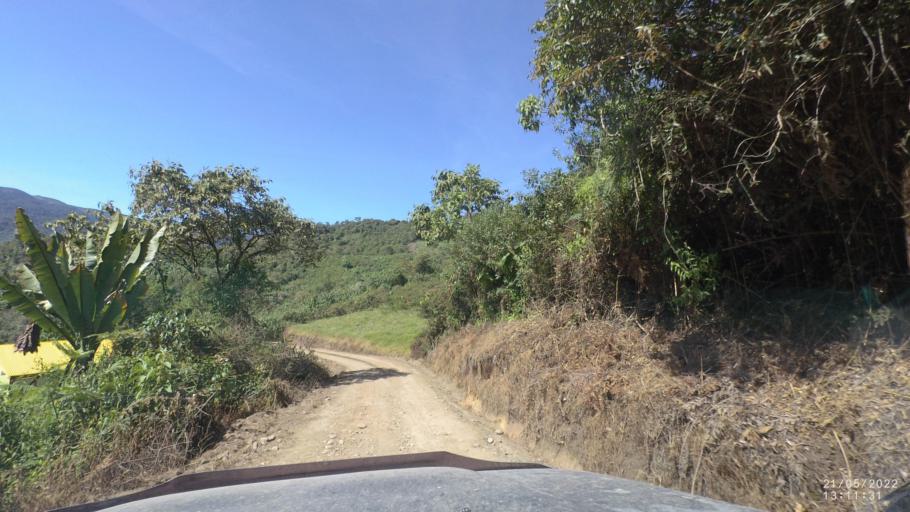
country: BO
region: Cochabamba
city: Colomi
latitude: -17.1394
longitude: -65.9423
